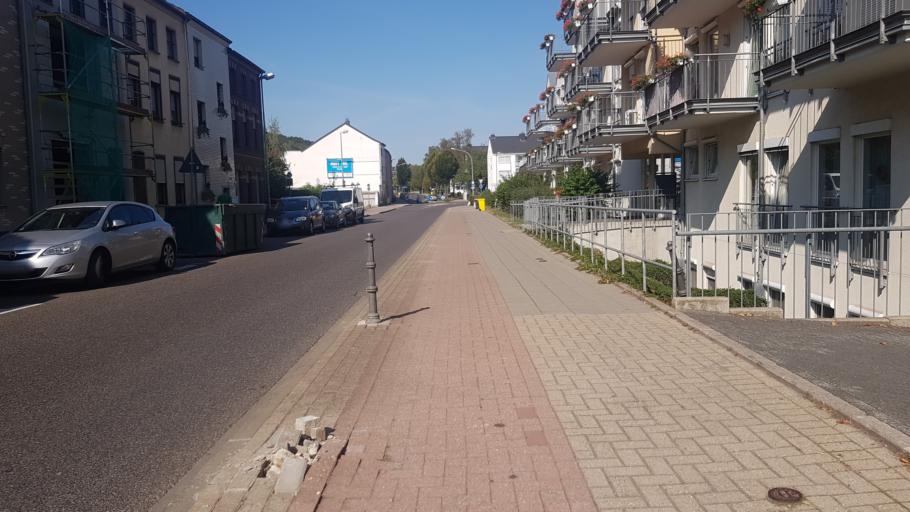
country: DE
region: North Rhine-Westphalia
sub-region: Regierungsbezirk Koln
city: Eschweiler
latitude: 50.8165
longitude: 6.2533
